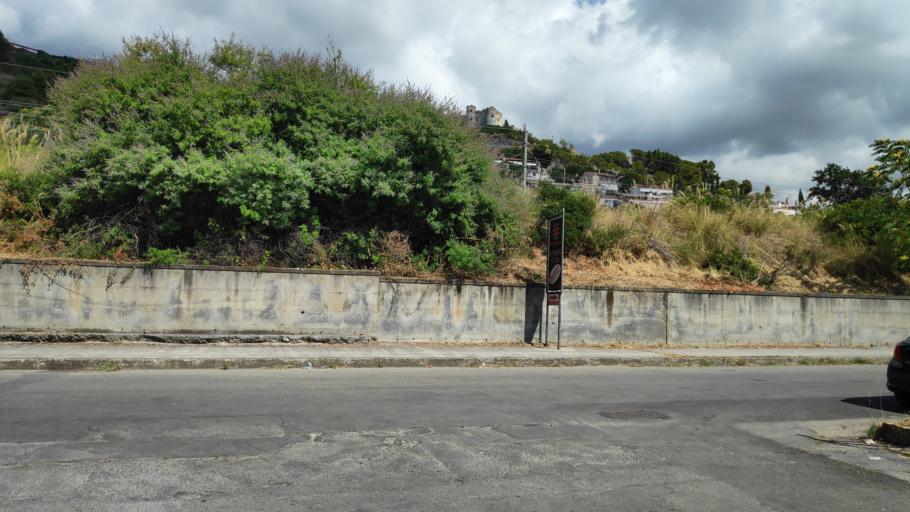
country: IT
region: Calabria
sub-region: Provincia di Cosenza
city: Praia a Mare
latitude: 39.8745
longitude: 15.7870
